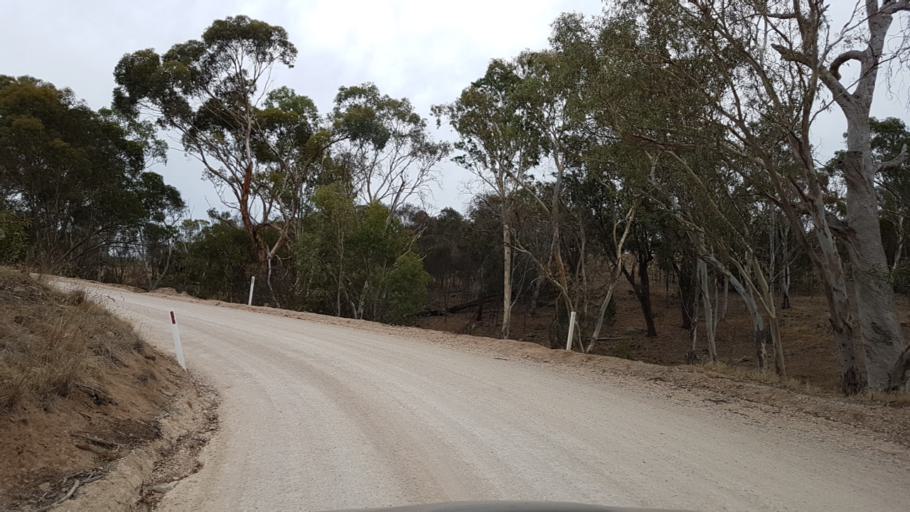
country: AU
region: South Australia
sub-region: Mount Barker
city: Callington
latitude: -35.0029
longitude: 139.0277
